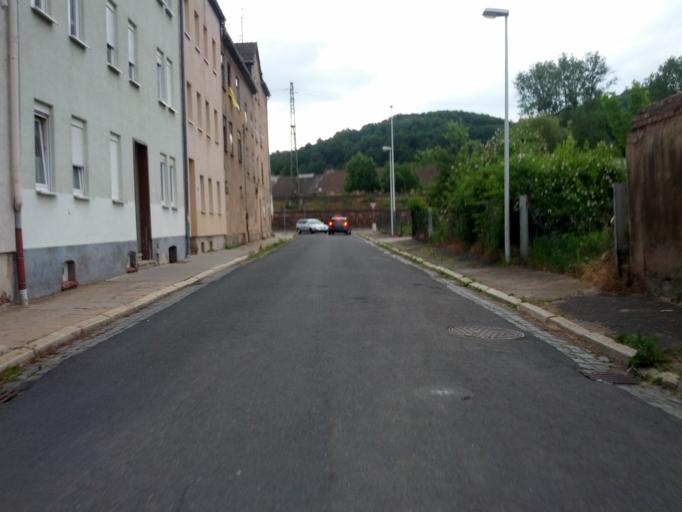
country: DE
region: Thuringia
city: Eisenach
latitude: 50.9802
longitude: 10.3124
